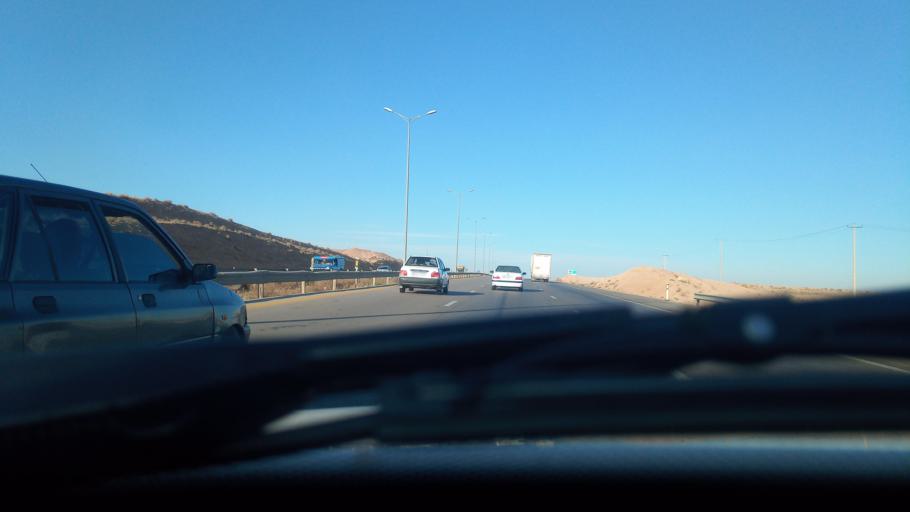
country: IR
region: Razavi Khorasan
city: Mashhad
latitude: 36.0644
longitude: 59.7277
